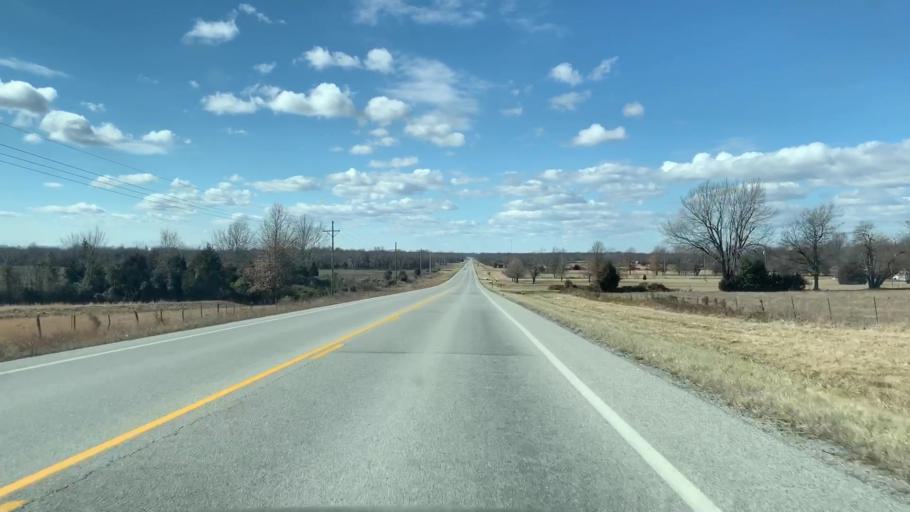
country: US
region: Kansas
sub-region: Cherokee County
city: Columbus
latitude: 37.1782
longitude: -94.7898
